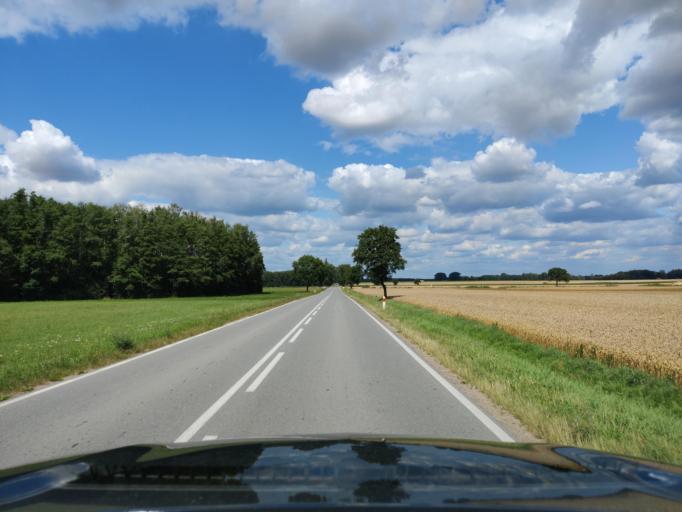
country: PL
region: Masovian Voivodeship
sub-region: Powiat wegrowski
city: Grebkow
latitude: 52.3129
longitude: 21.9365
